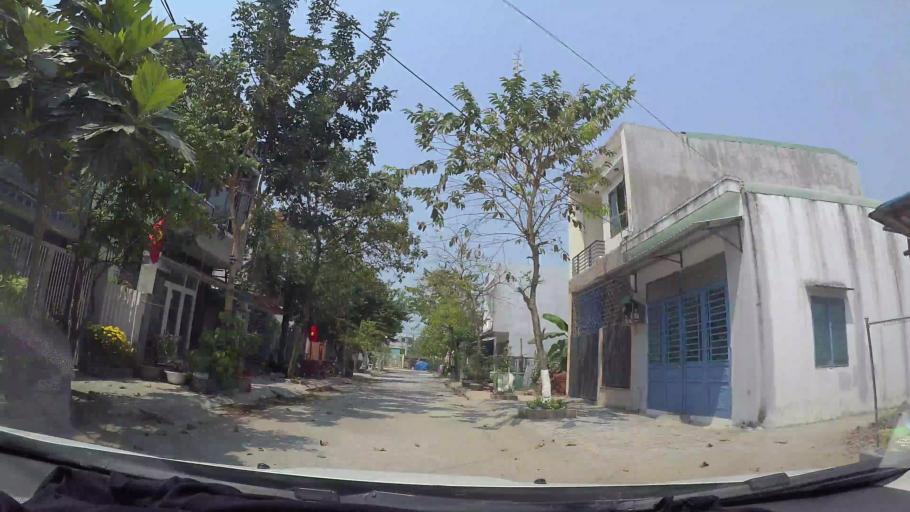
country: VN
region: Da Nang
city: Cam Le
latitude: 15.9961
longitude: 108.2044
